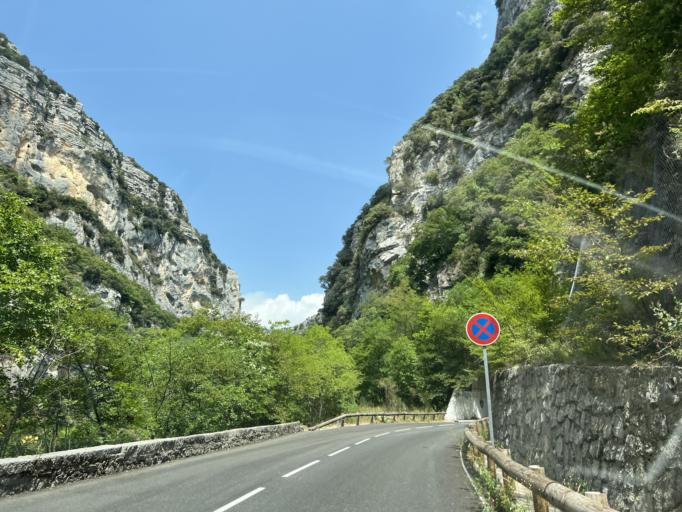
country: FR
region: Provence-Alpes-Cote d'Azur
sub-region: Departement des Alpes-Maritimes
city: Tourrettes-sur-Loup
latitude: 43.7356
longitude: 6.9989
